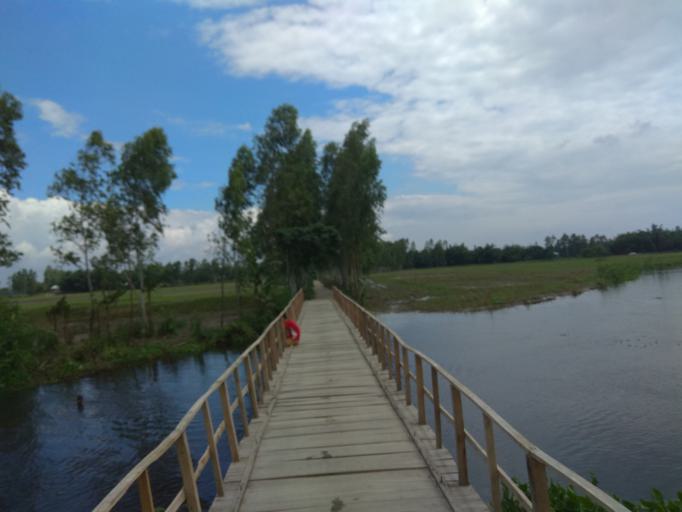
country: IN
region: West Bengal
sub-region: Koch Bihar
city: Haldibari
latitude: 26.1182
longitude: 88.9259
